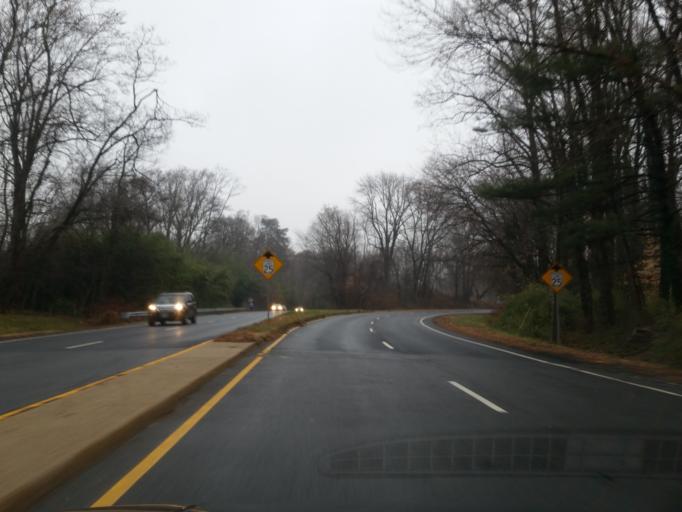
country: US
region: Maryland
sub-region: Montgomery County
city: Brookmont
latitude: 38.9249
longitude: -77.1260
